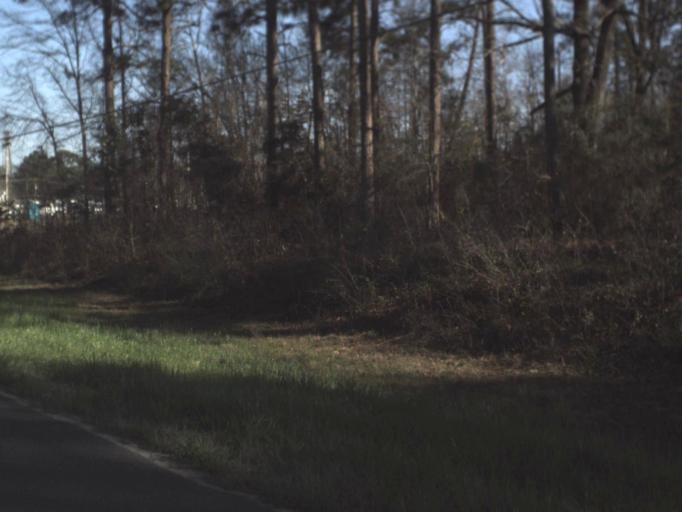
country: US
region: Florida
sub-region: Jackson County
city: Marianna
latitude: 30.7841
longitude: -85.2737
